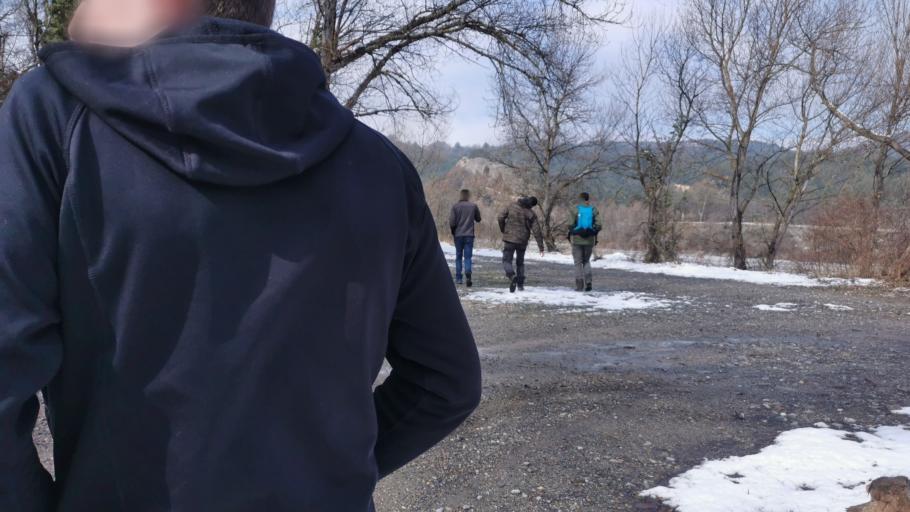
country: FR
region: Provence-Alpes-Cote d'Azur
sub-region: Departement des Alpes-de-Haute-Provence
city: Mallemoisson
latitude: 44.0650
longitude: 6.1758
